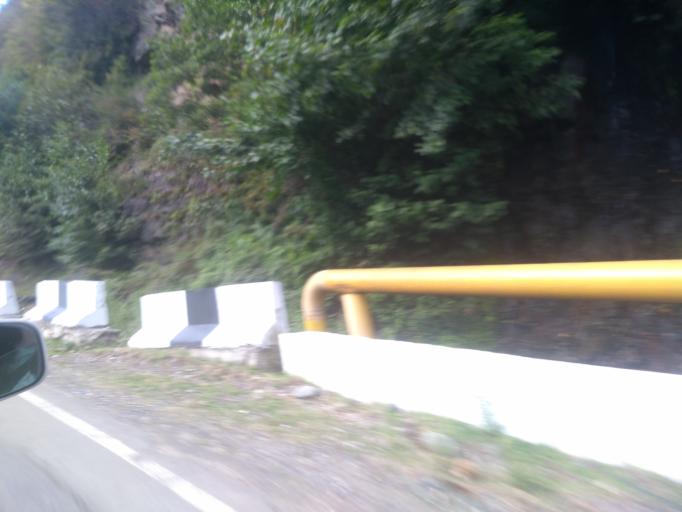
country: GE
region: Ajaria
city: Khelvachauri
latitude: 41.5513
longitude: 41.7019
